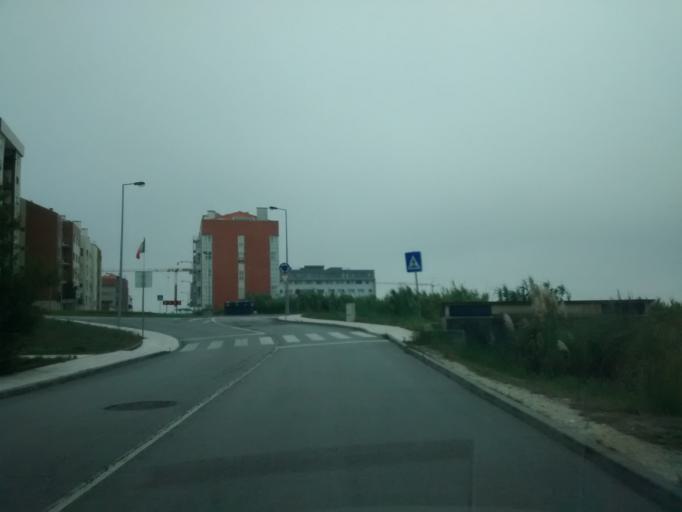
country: PT
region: Aveiro
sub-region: Aveiro
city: Aveiro
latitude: 40.6491
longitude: -8.6457
